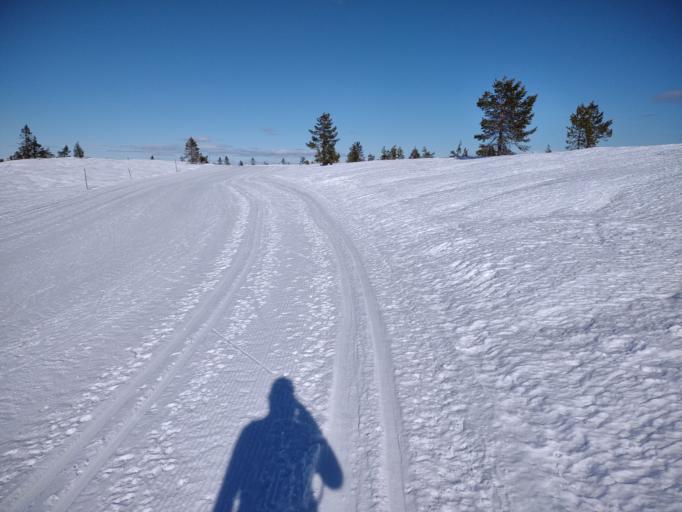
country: NO
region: Buskerud
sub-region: Flesberg
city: Lampeland
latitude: 59.7769
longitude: 9.3987
